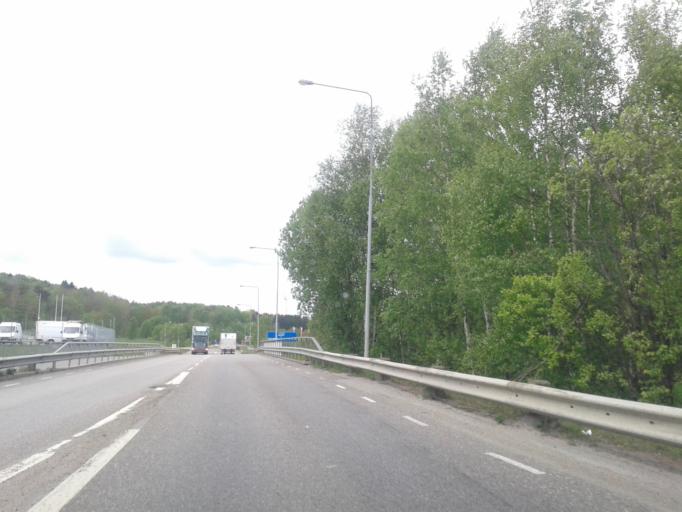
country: SE
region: Vaestra Goetaland
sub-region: Goteborg
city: Hammarkullen
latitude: 57.7874
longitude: 12.0485
